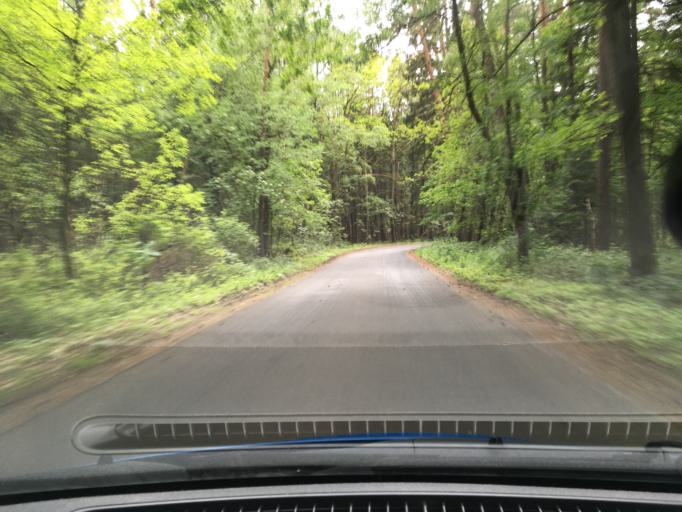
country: DE
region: Lower Saxony
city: Rehlingen
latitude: 53.1025
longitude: 10.2361
